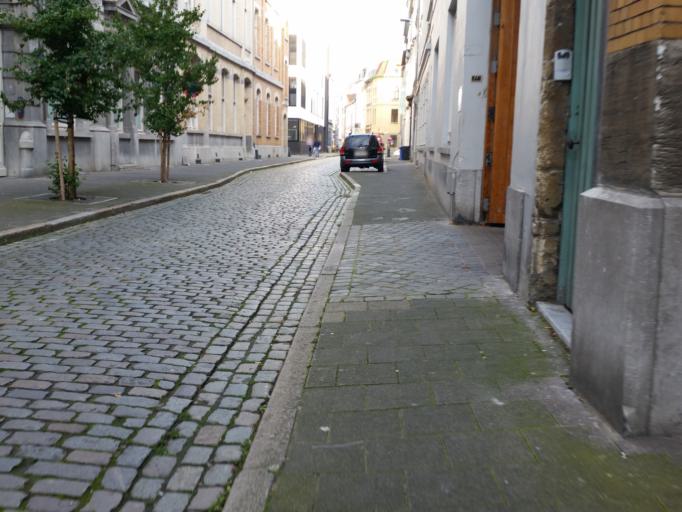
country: BE
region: Flanders
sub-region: Provincie Antwerpen
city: Antwerpen
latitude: 51.2227
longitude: 4.4069
